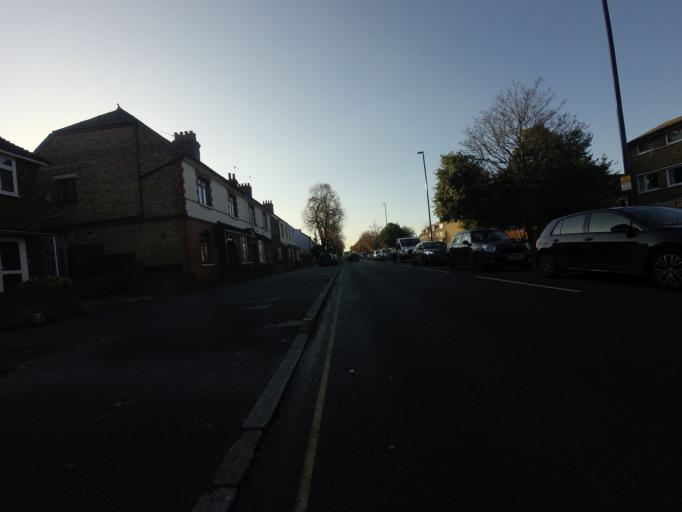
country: GB
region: England
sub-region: Greater London
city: Feltham
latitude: 51.4566
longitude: -0.4145
